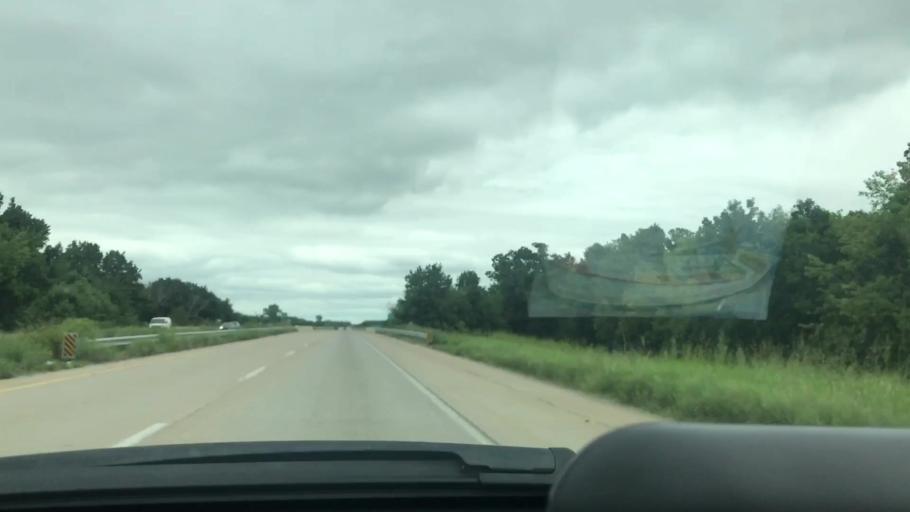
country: US
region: Oklahoma
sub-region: Mayes County
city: Chouteau
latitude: 36.2055
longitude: -95.3408
